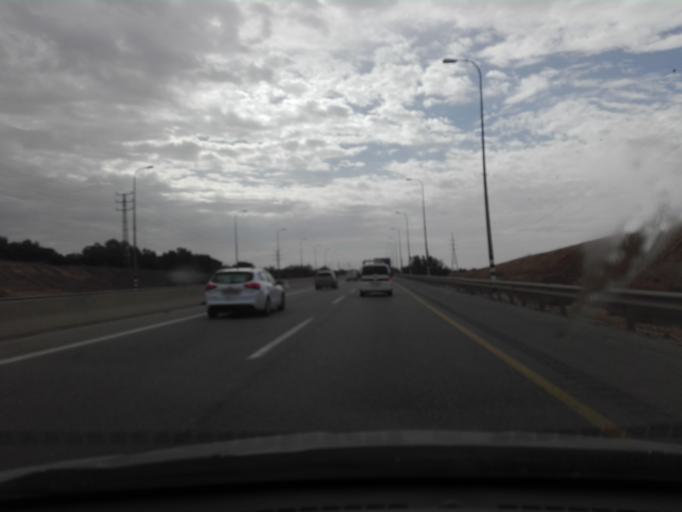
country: IL
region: Southern District
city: Lehavim
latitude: 31.3402
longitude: 34.7891
